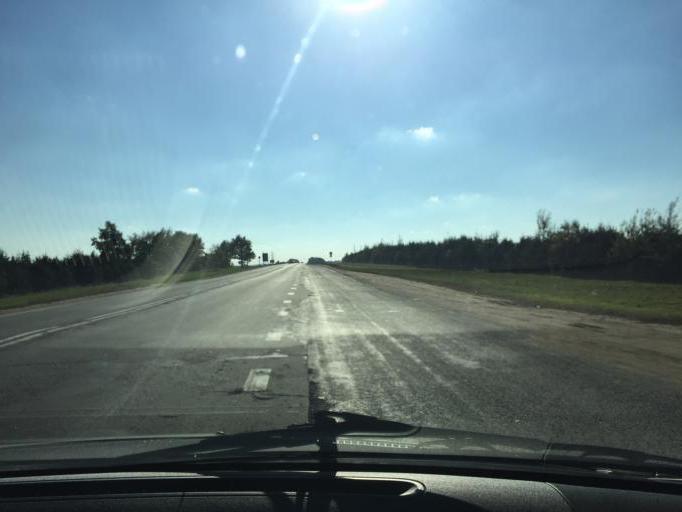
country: BY
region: Minsk
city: Slutsk
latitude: 52.9843
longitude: 27.5051
